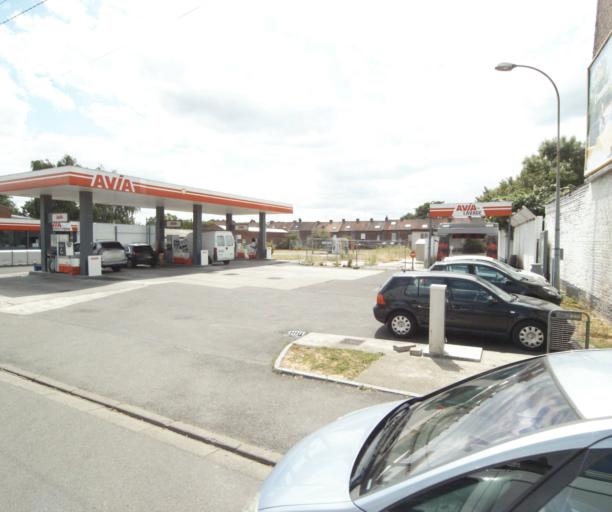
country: FR
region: Nord-Pas-de-Calais
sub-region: Departement du Nord
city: Mouvaux
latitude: 50.6969
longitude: 3.1419
